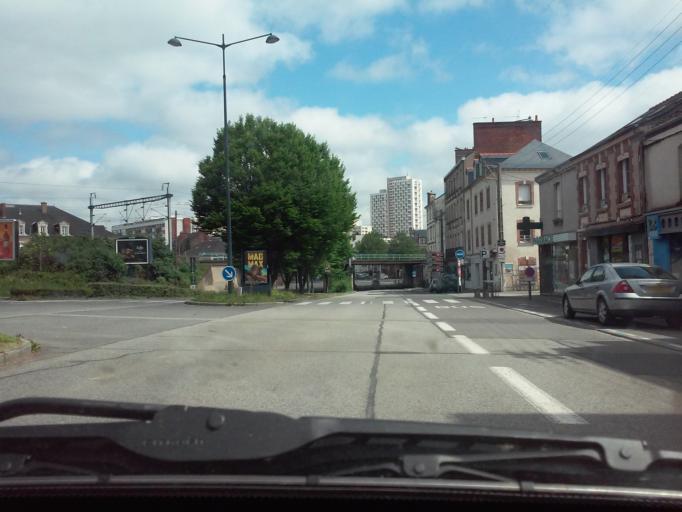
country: FR
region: Brittany
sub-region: Departement d'Ille-et-Vilaine
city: Rennes
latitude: 48.1007
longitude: -1.6855
